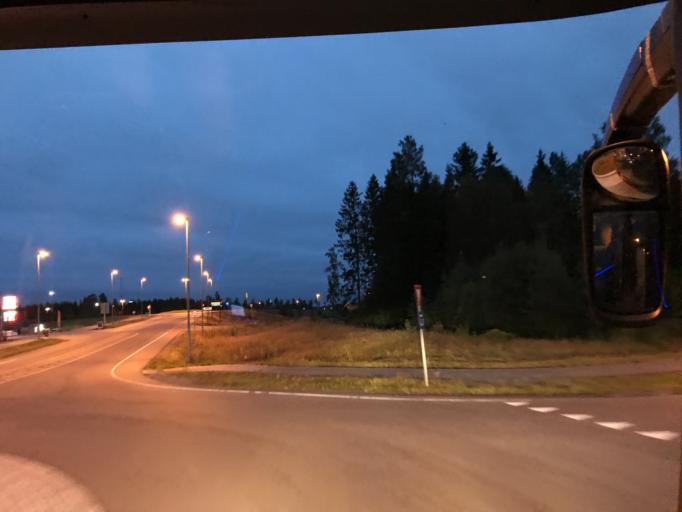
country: NO
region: Akershus
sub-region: Eidsvoll
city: Eidsvoll
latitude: 60.3916
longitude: 11.2131
